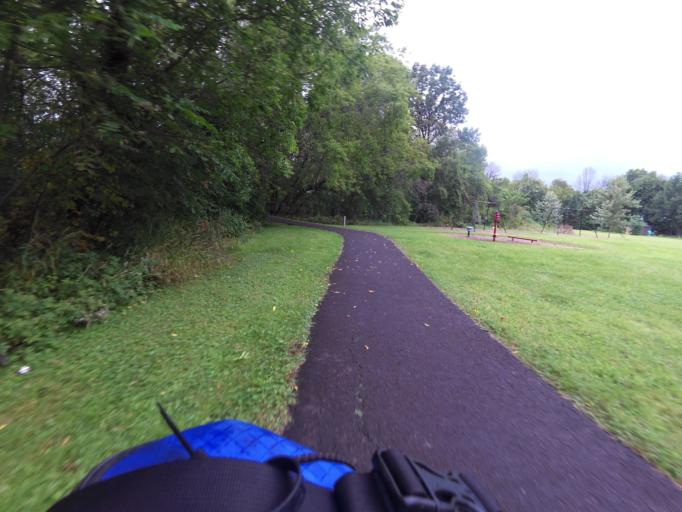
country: CA
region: Ontario
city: Ottawa
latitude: 45.2293
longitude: -75.4747
